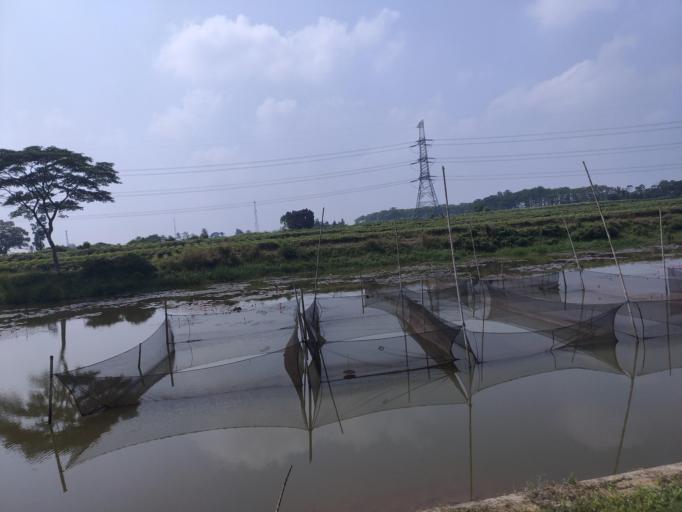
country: ID
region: West Java
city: Ciampea
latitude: -6.4865
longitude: 106.6837
